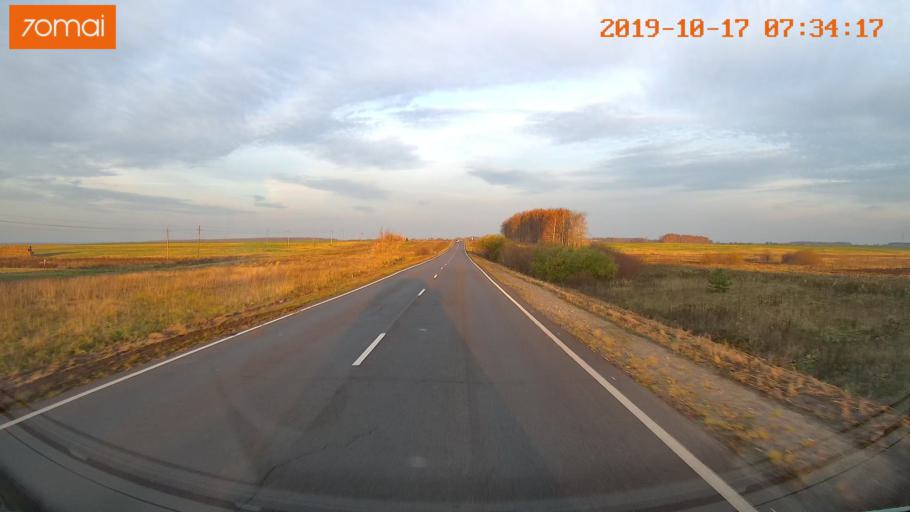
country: RU
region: Ivanovo
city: Gavrilov Posad
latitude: 56.4159
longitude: 39.9448
